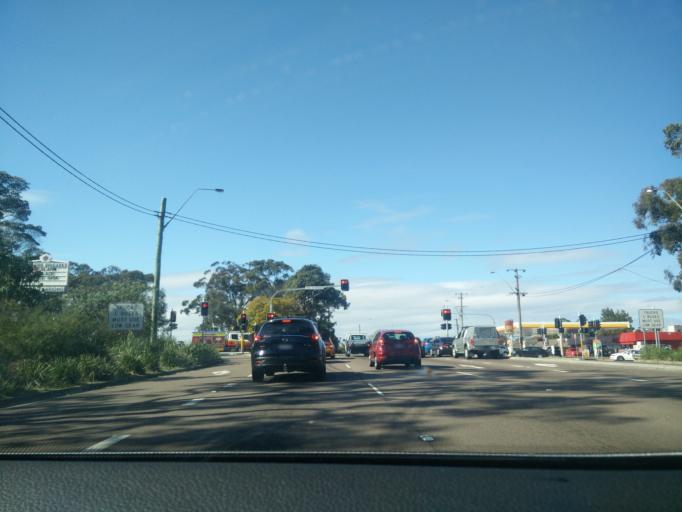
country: AU
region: New South Wales
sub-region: Gosford Shire
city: Point Clare
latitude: -33.4334
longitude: 151.2962
